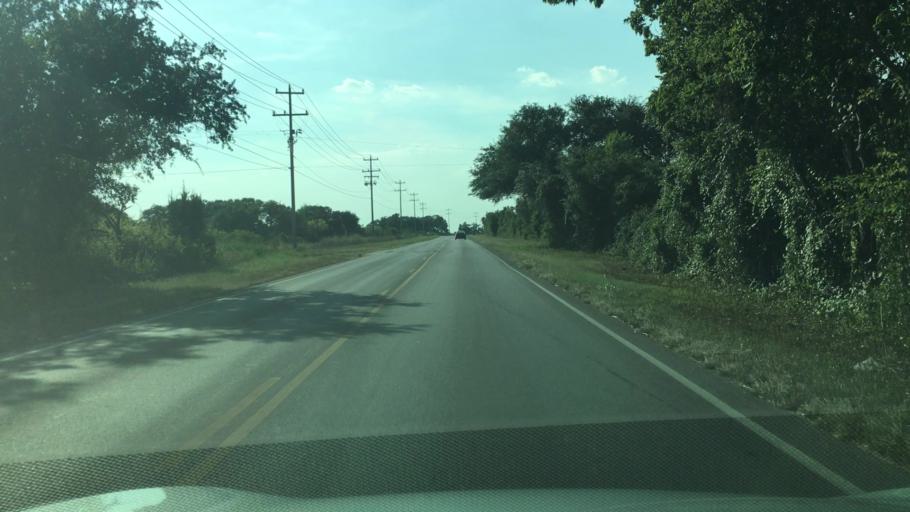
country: US
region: Texas
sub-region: Hays County
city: Buda
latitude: 30.0989
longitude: -97.9341
